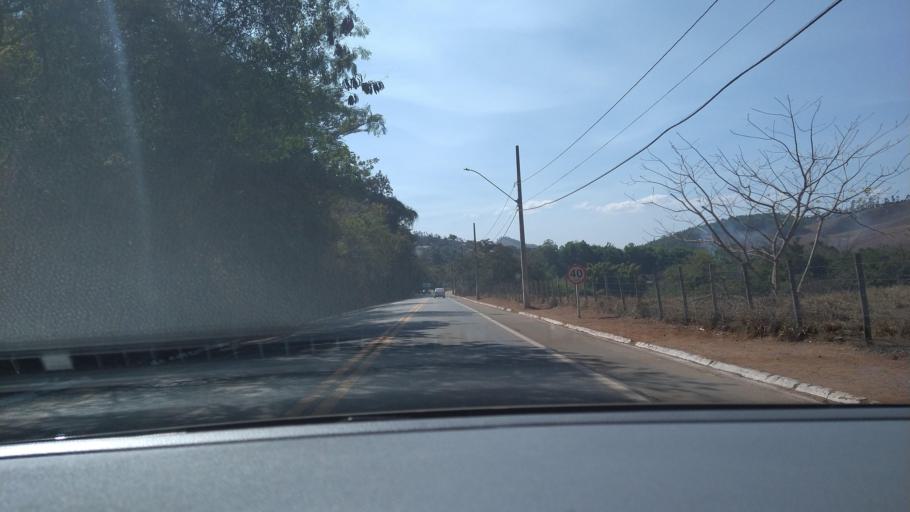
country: BR
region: Minas Gerais
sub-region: Rio Piracicaba
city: Rio Piracicaba
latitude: -19.9245
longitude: -43.1641
